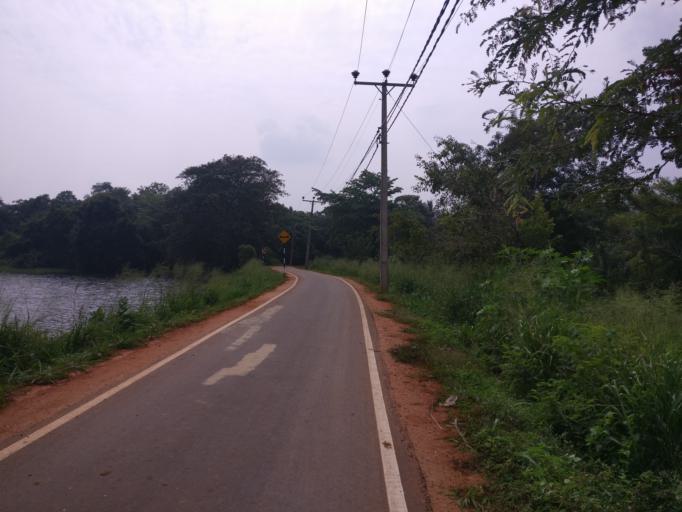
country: LK
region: Central
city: Dambulla
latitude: 7.8363
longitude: 80.6480
